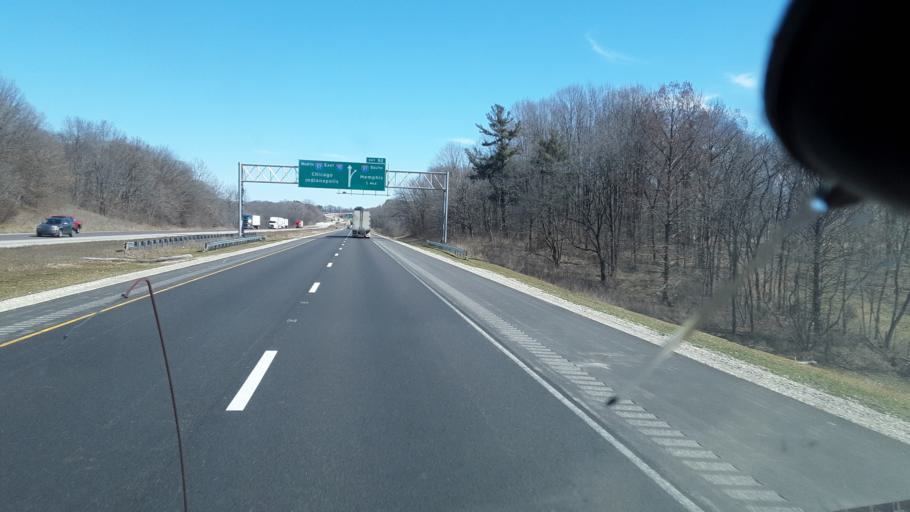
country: US
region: Illinois
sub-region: Effingham County
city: Effingham
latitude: 39.0879
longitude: -88.6034
